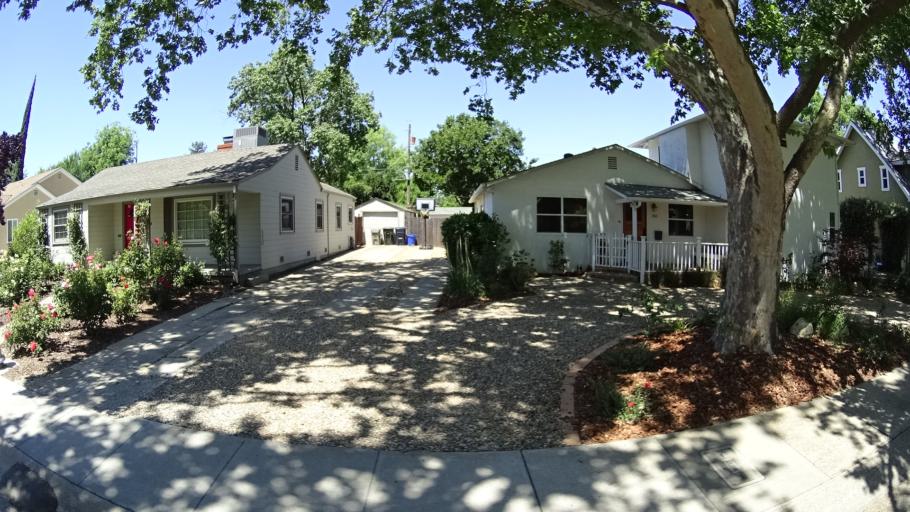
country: US
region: California
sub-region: Sacramento County
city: Sacramento
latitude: 38.5624
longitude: -121.4360
